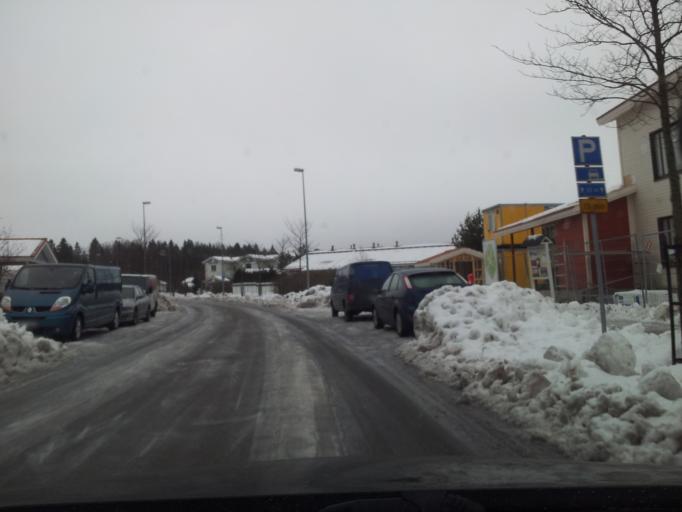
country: FI
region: Uusimaa
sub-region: Helsinki
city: Espoo
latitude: 60.1574
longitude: 24.5510
